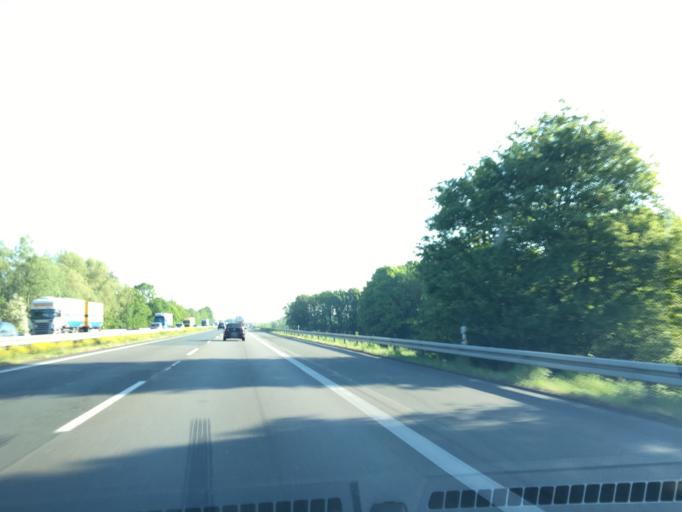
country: DE
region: North Rhine-Westphalia
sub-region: Regierungsbezirk Munster
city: Greven
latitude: 52.0392
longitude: 7.6069
